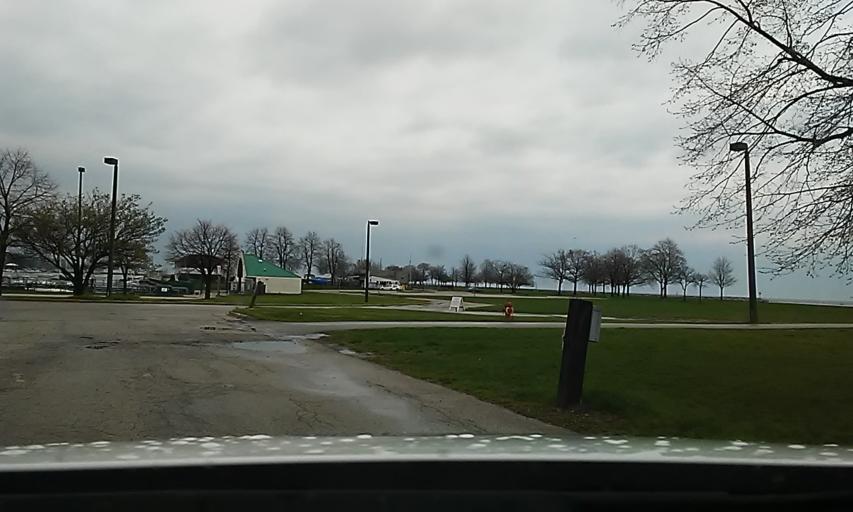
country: US
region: Wisconsin
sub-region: Milwaukee County
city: Milwaukee
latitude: 43.0441
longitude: -87.8889
